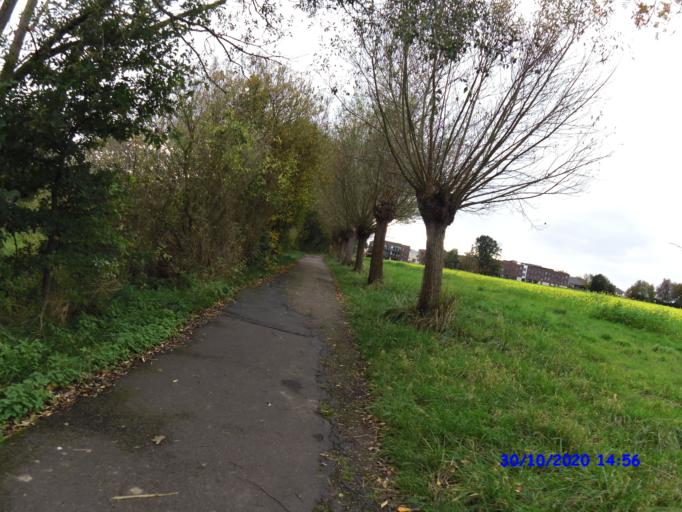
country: BE
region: Flanders
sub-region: Provincie Vlaams-Brabant
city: Landen
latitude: 50.7616
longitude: 5.0840
